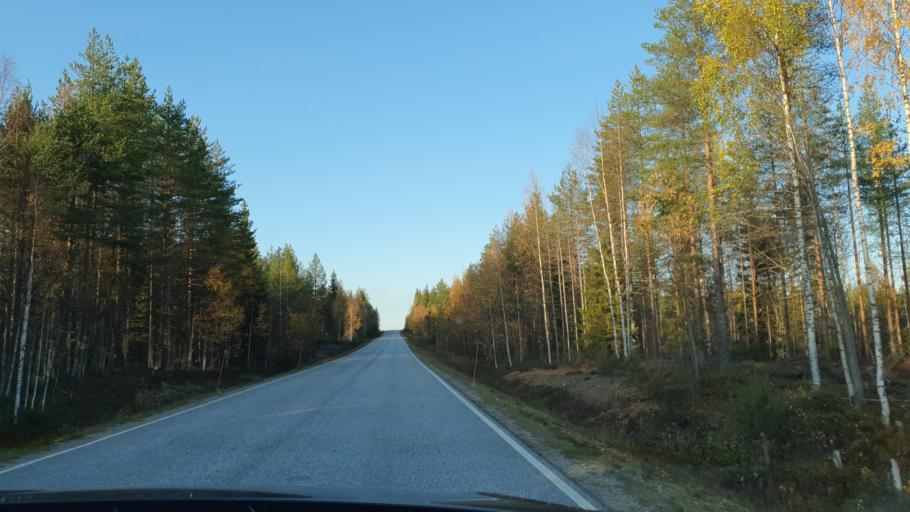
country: FI
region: Kainuu
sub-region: Kehys-Kainuu
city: Kuhmo
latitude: 64.3465
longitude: 29.4877
